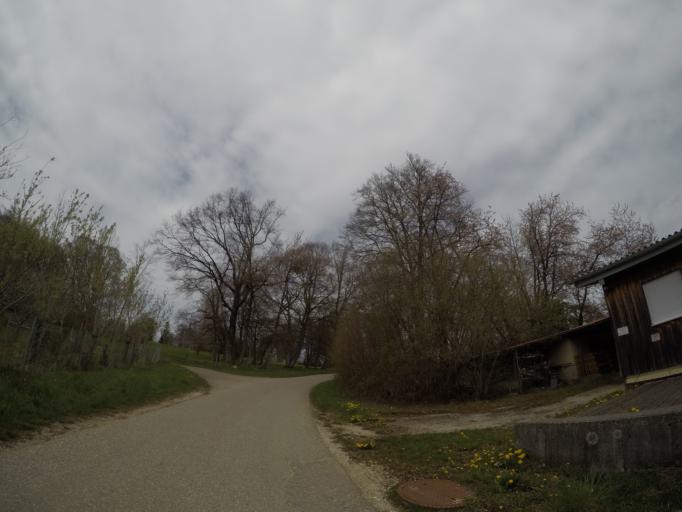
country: DE
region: Baden-Wuerttemberg
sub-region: Tuebingen Region
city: Laichingen
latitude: 48.4764
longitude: 9.6950
